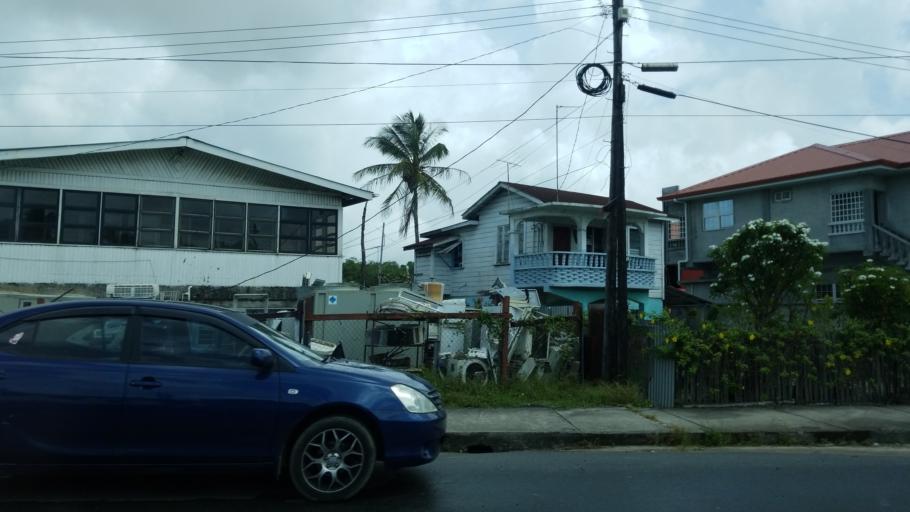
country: GY
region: Demerara-Mahaica
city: Georgetown
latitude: 6.7710
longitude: -58.1753
